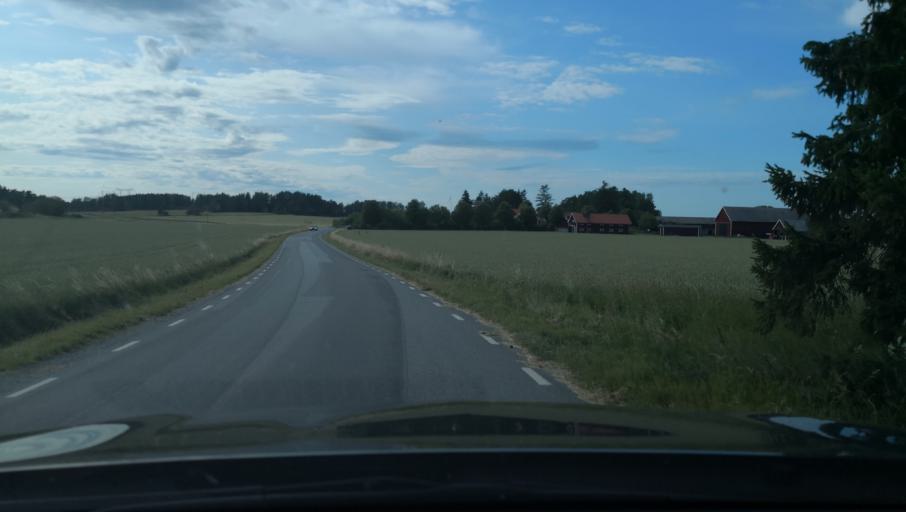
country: SE
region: Uppsala
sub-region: Habo Kommun
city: Balsta
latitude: 59.6714
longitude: 17.4382
